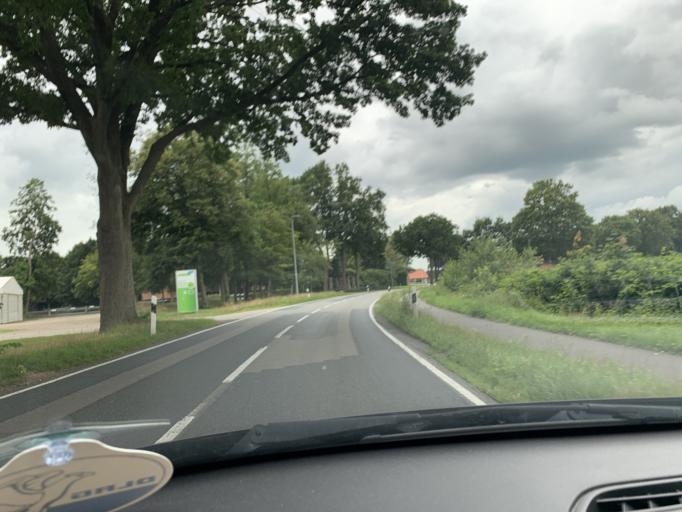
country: DE
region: Lower Saxony
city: Edewecht
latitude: 53.1288
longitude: 7.8968
